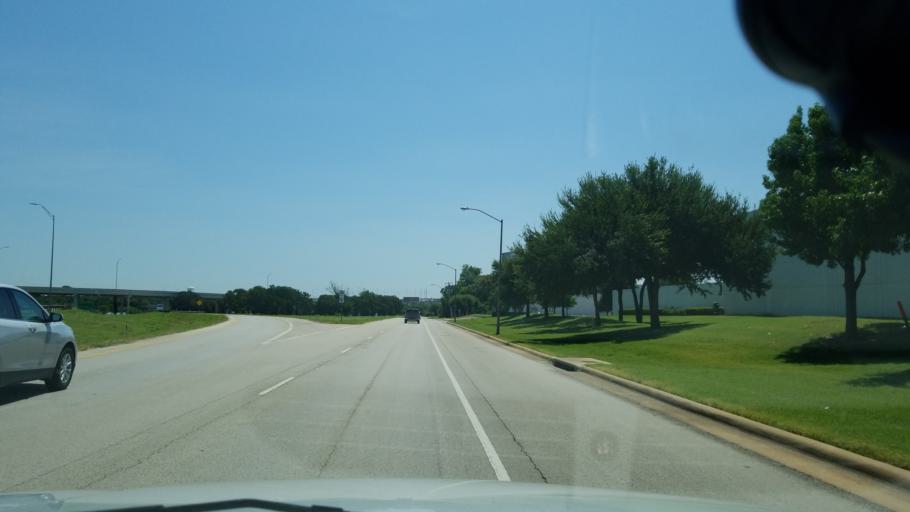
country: US
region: Texas
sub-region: Tarrant County
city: Euless
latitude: 32.8353
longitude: -97.0434
